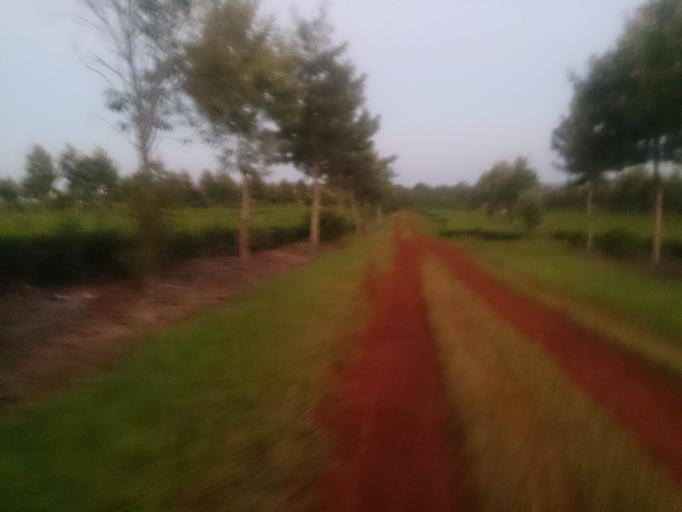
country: AR
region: Misiones
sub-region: Departamento de Obera
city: Obera
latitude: -27.4439
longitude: -55.0859
